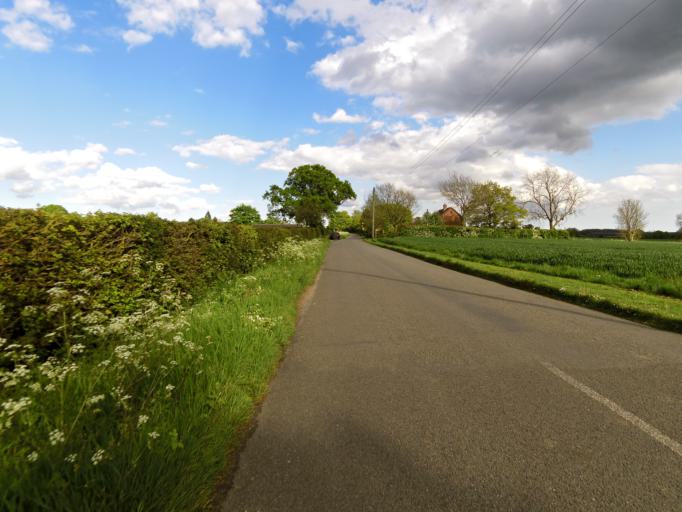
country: GB
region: England
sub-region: Suffolk
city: Elmswell
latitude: 52.1997
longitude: 0.9471
